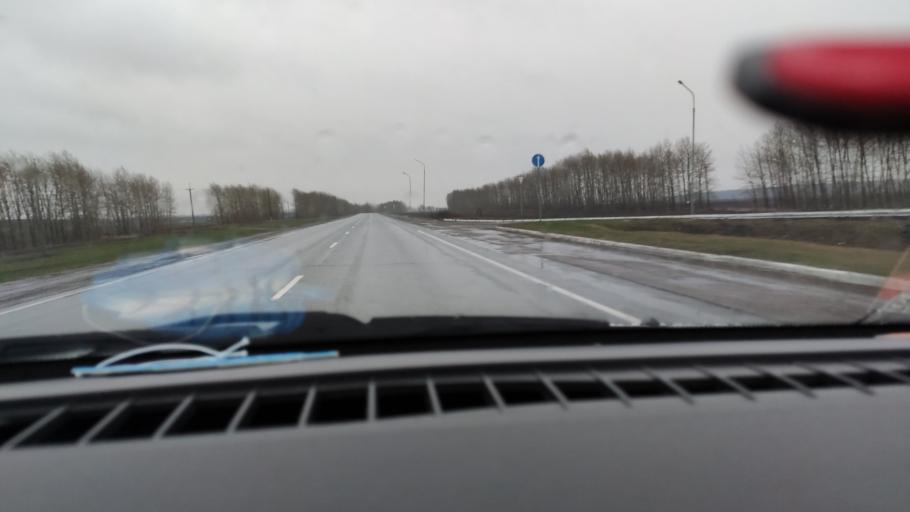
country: RU
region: Tatarstan
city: Mendeleyevsk
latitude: 55.9146
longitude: 52.2719
